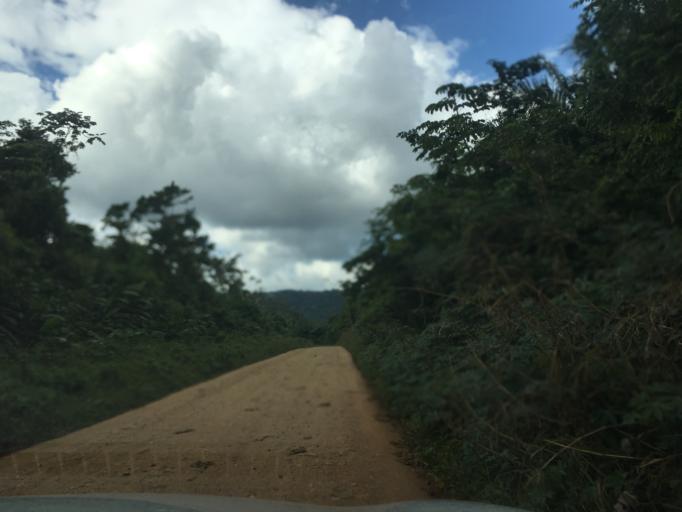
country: BZ
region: Stann Creek
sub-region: Dangriga
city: Dangriga
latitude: 16.9379
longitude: -88.3671
